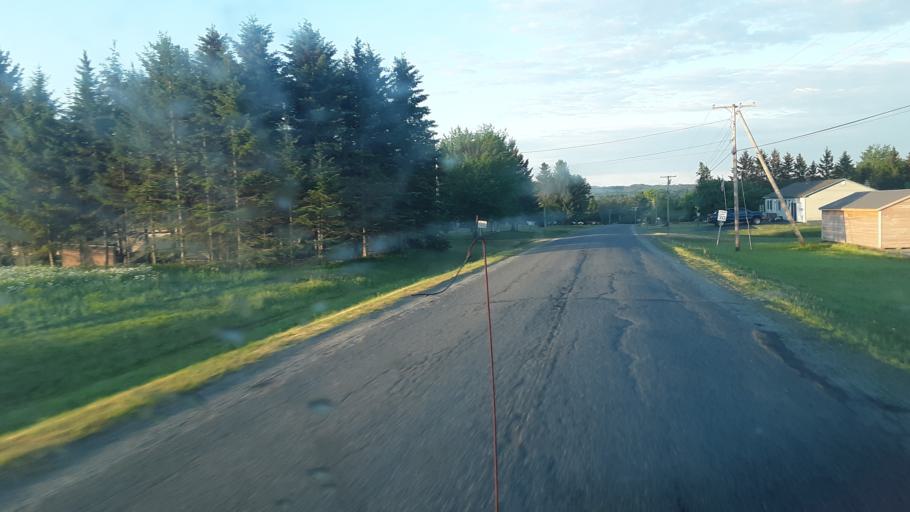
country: US
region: Maine
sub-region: Aroostook County
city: Presque Isle
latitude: 46.7593
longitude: -68.1021
